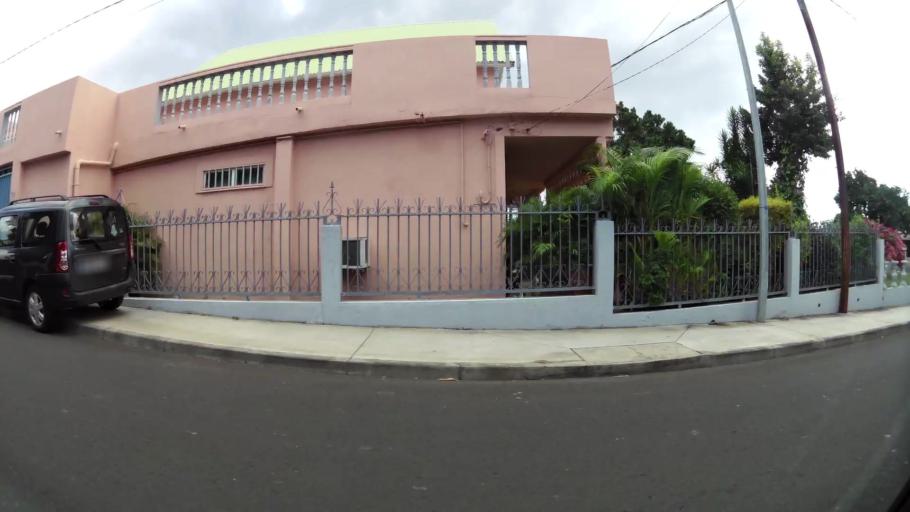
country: RE
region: Reunion
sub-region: Reunion
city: Saint-Denis
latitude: -20.8915
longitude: 55.4744
